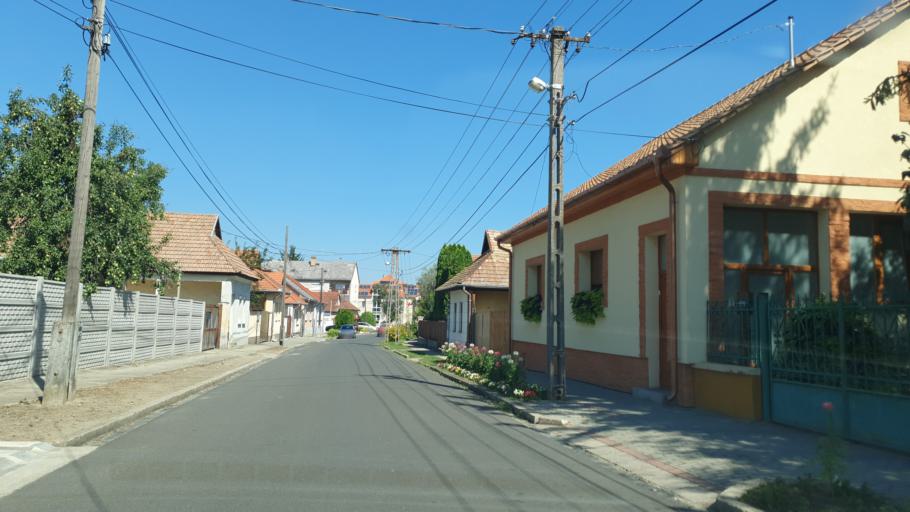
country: HU
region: Nograd
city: Szecseny
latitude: 48.0799
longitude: 19.5149
